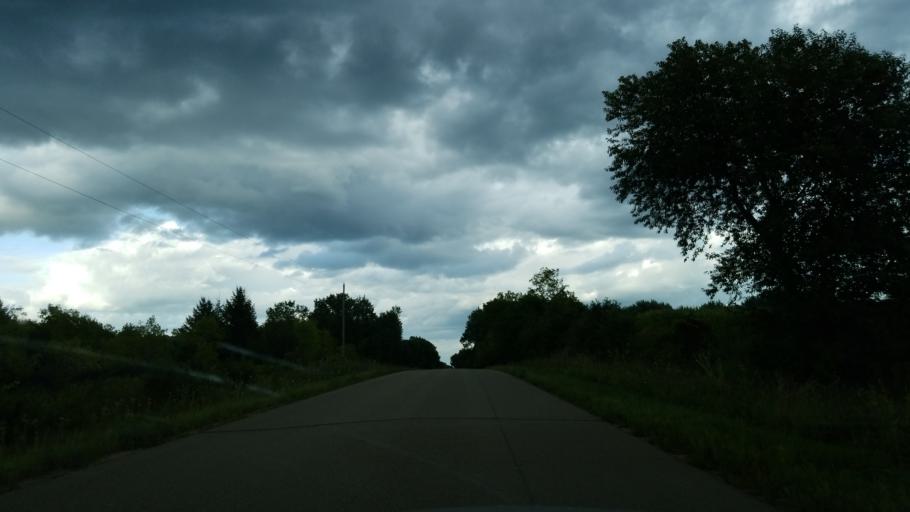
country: US
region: Minnesota
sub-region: Washington County
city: Afton
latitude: 44.8802
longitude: -92.7444
